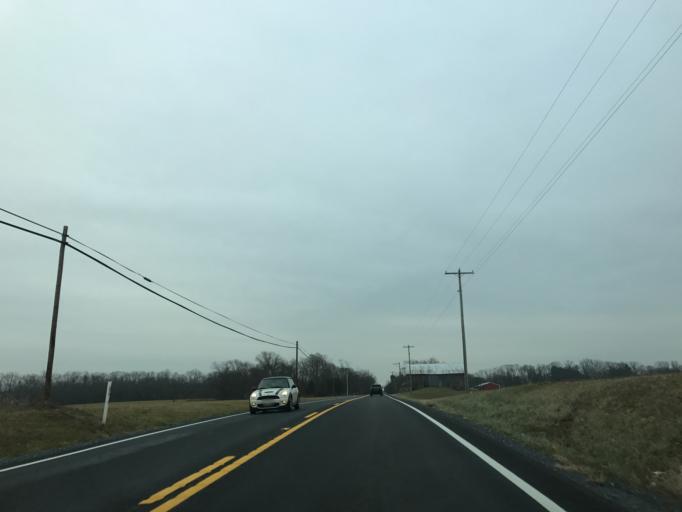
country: US
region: Maryland
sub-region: Frederick County
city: Emmitsburg
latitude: 39.6887
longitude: -77.2677
